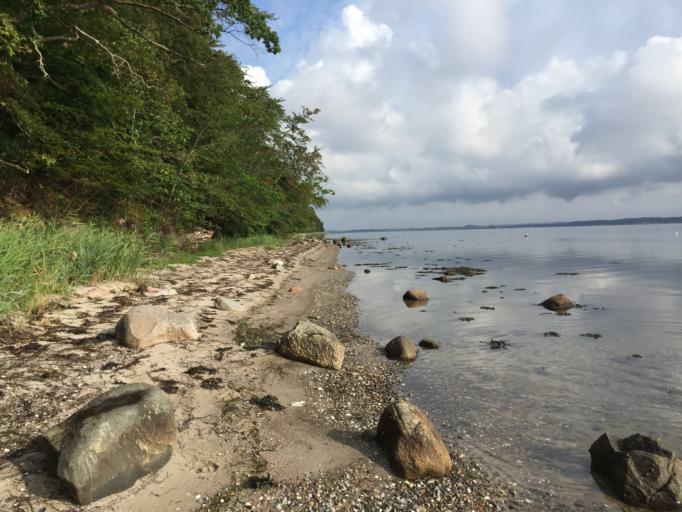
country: DK
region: South Denmark
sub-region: Assens Kommune
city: Harby
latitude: 55.1394
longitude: 10.0352
